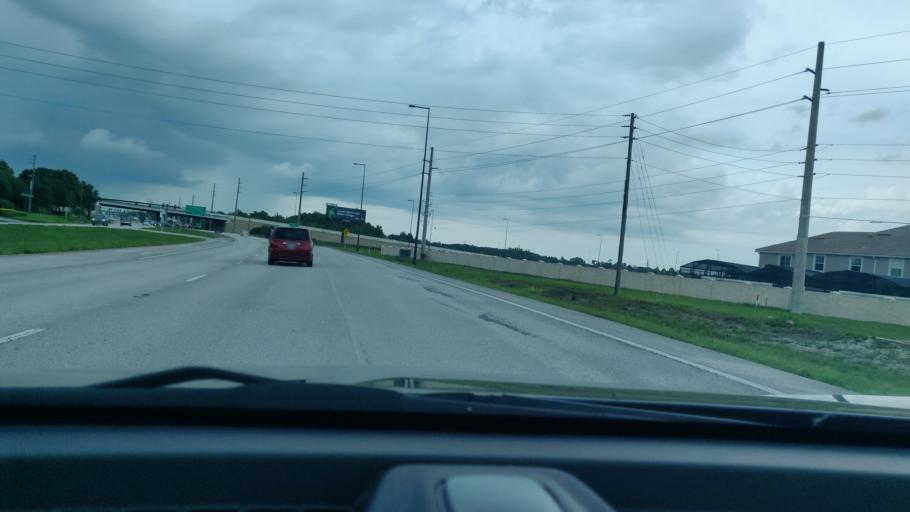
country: US
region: Florida
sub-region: Osceola County
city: Celebration
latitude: 28.3379
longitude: -81.4801
